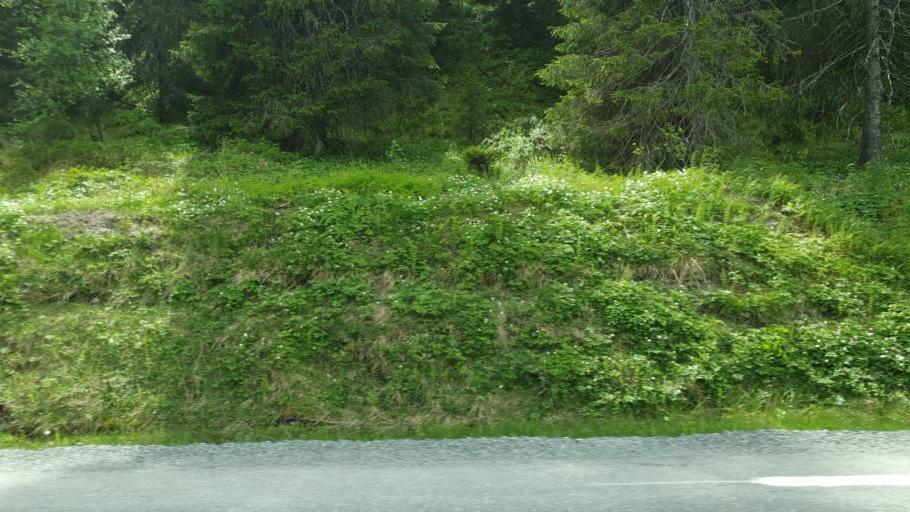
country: NO
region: Nord-Trondelag
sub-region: Leksvik
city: Leksvik
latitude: 63.6924
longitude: 10.5126
